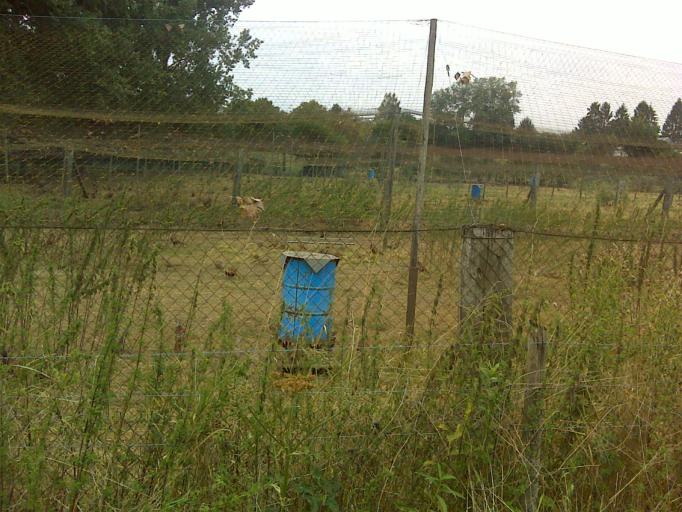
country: FR
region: Nord-Pas-de-Calais
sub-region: Departement du Nord
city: Bousies
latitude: 50.1017
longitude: 3.6379
